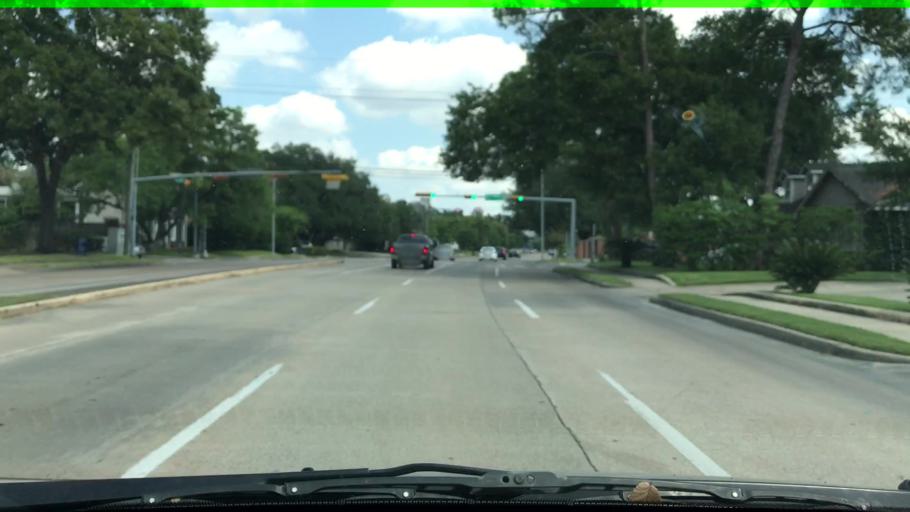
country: US
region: Texas
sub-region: Harris County
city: Hunters Creek Village
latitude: 29.7500
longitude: -95.4931
